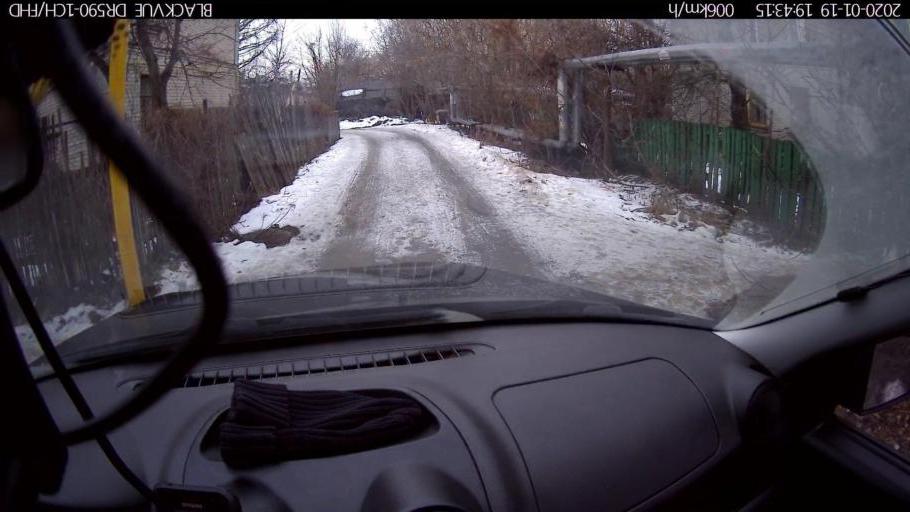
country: RU
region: Nizjnij Novgorod
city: Nizhniy Novgorod
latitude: 56.3011
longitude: 43.9093
